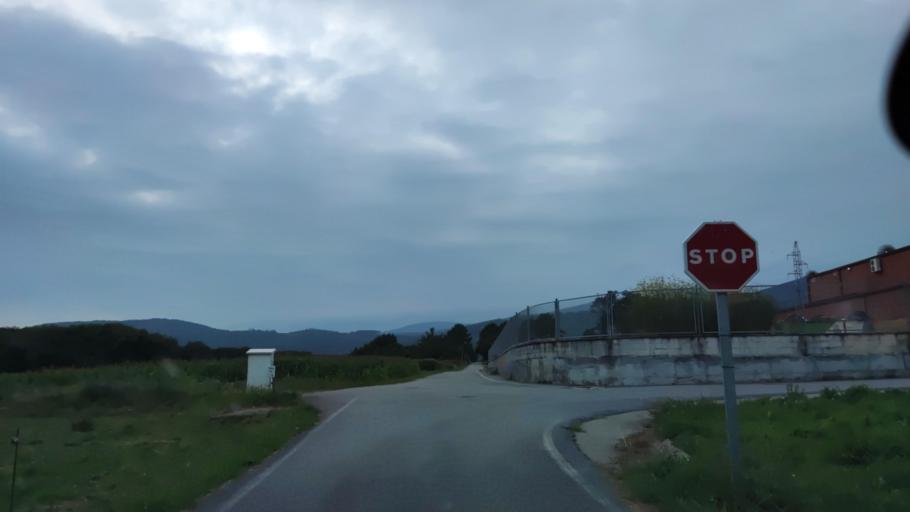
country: ES
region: Galicia
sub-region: Provincia da Coruna
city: Padron
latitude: 42.7136
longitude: -8.6975
